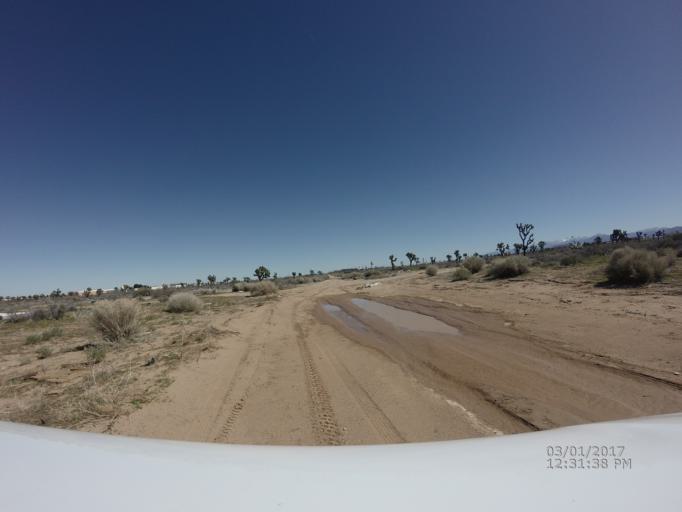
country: US
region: California
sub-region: Los Angeles County
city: Desert View Highlands
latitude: 34.6385
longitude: -118.1569
